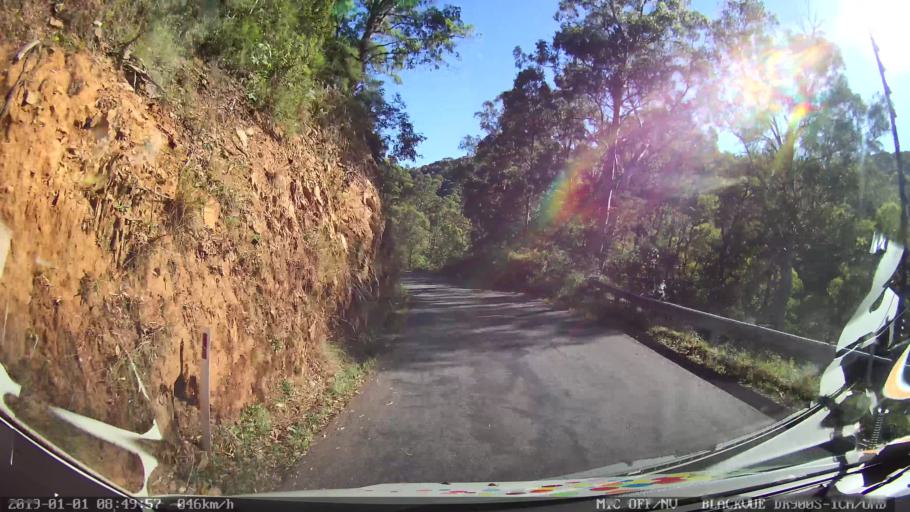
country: AU
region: New South Wales
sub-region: Snowy River
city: Jindabyne
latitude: -36.2792
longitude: 148.2018
